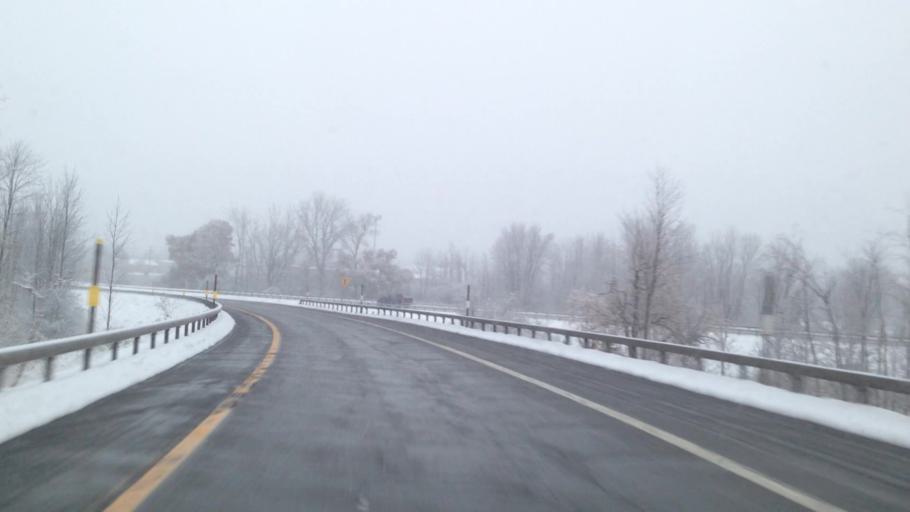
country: US
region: New York
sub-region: Onondaga County
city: East Syracuse
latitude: 43.0556
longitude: -76.0517
